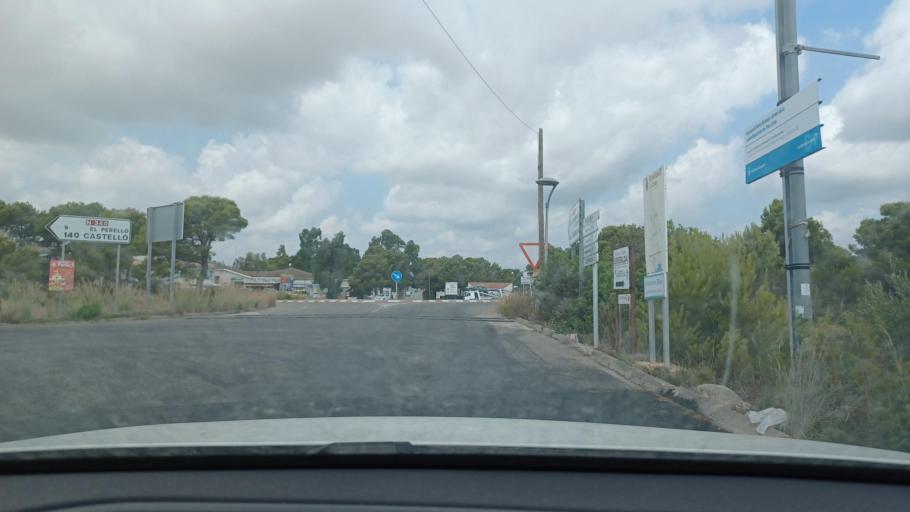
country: ES
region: Catalonia
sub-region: Provincia de Tarragona
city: l'Ametlla de Mar
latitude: 40.9080
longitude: 0.8110
